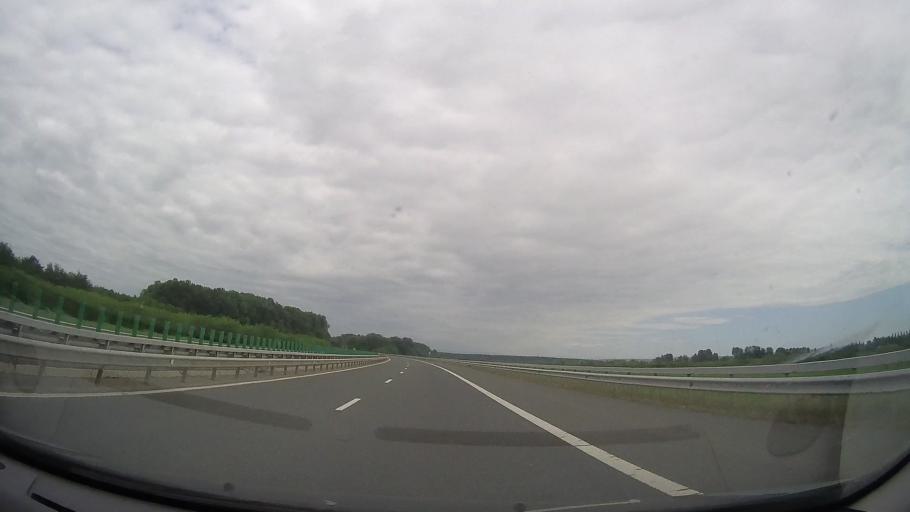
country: RO
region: Prahova
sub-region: Comuna Rafov
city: Rafov
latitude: 44.8812
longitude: 26.1352
